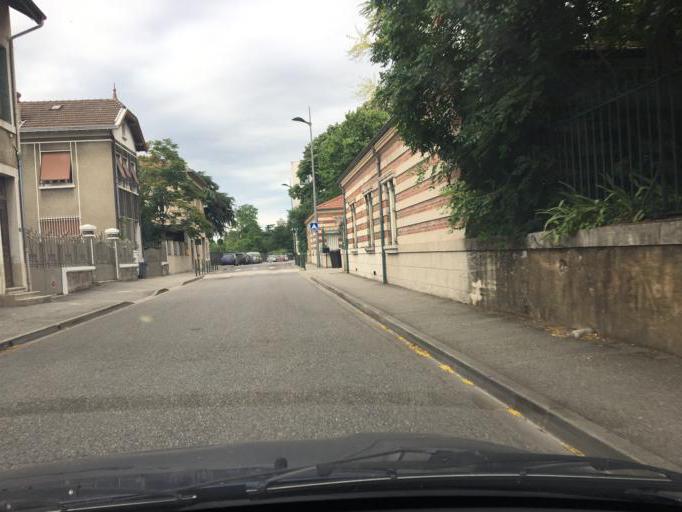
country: FR
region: Rhone-Alpes
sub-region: Departement de l'Ardeche
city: Guilherand-Granges
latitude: 44.9263
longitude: 4.8859
